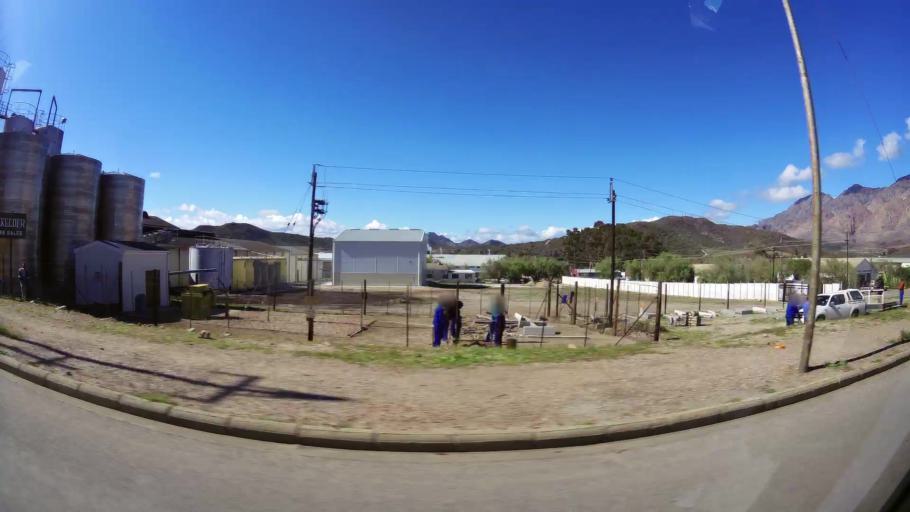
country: ZA
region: Western Cape
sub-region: Cape Winelands District Municipality
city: Ashton
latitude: -33.7774
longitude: 20.1318
